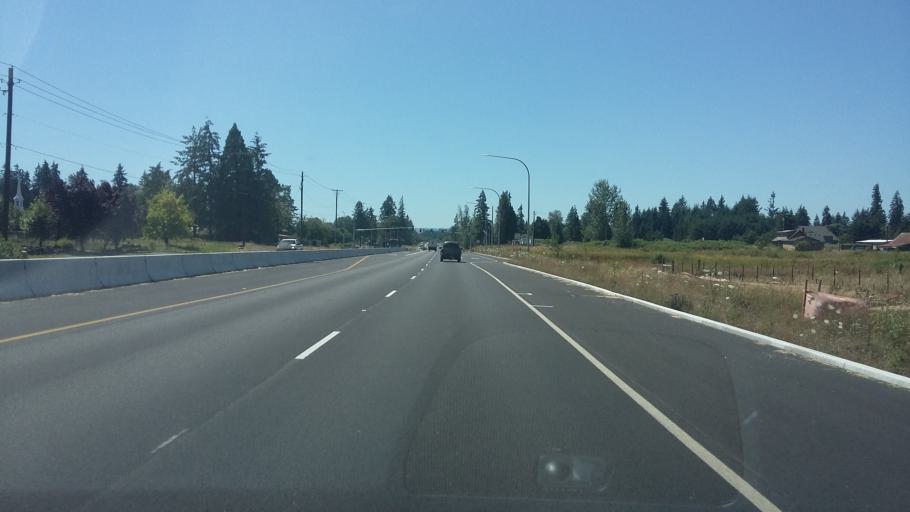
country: US
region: Washington
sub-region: Clark County
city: Dollar Corner
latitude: 45.7798
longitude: -122.6376
